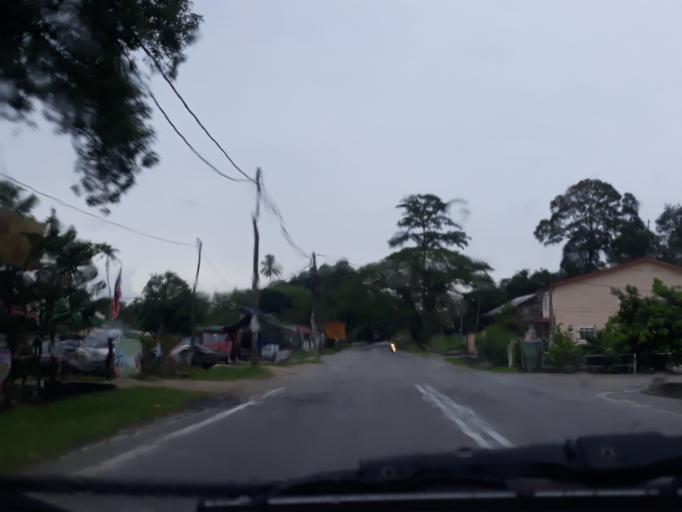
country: MY
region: Penang
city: Nibong Tebal
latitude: 5.2148
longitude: 100.6115
